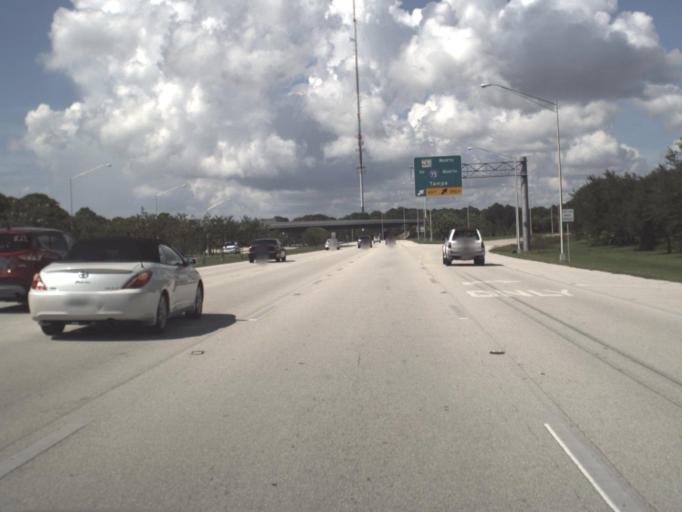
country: US
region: Florida
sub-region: Sarasota County
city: Laurel
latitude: 27.1460
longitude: -82.4622
